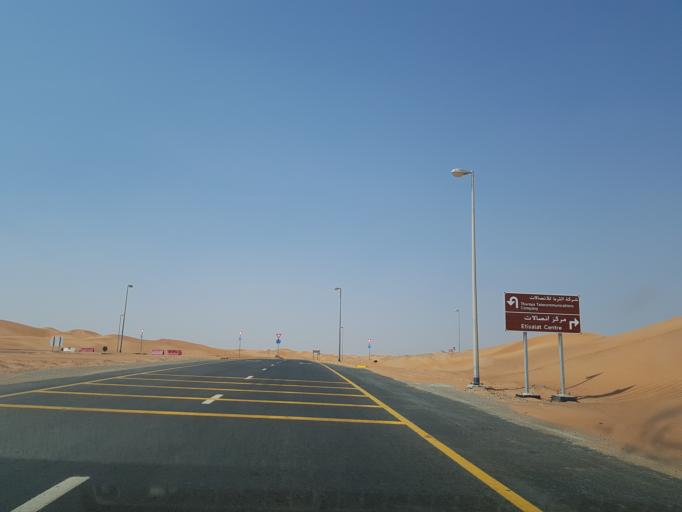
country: AE
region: Ash Shariqah
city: Adh Dhayd
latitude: 25.2505
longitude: 55.8200
